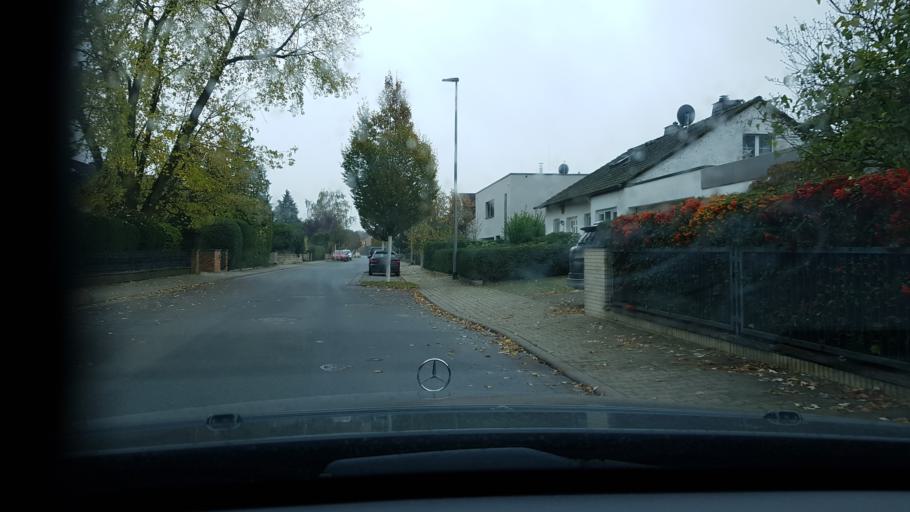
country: DE
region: Hesse
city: Schwalbach am Taunus
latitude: 50.1447
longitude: 8.5414
